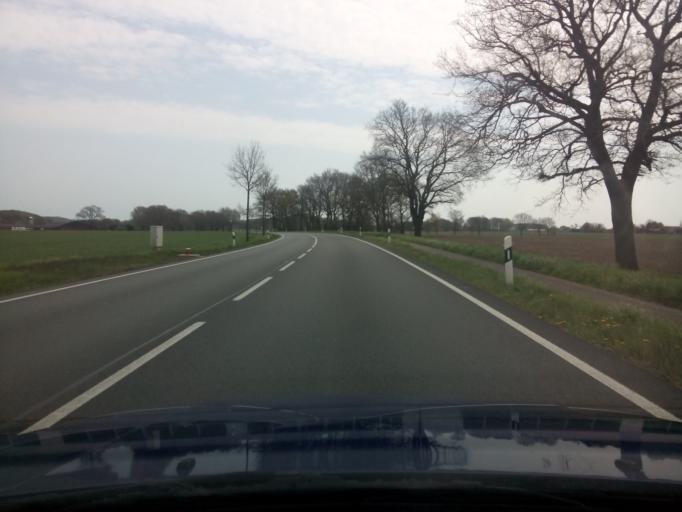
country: DE
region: Lower Saxony
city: Sustedt
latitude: 52.8396
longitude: 8.9049
